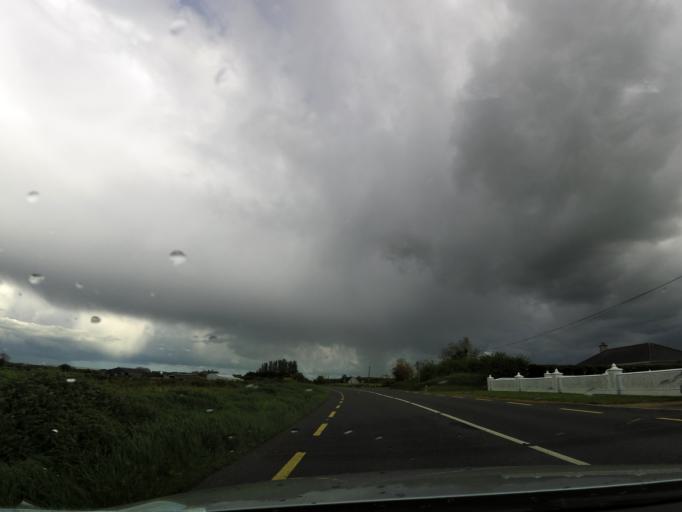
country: IE
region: Munster
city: Thurles
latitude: 52.7284
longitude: -7.8377
